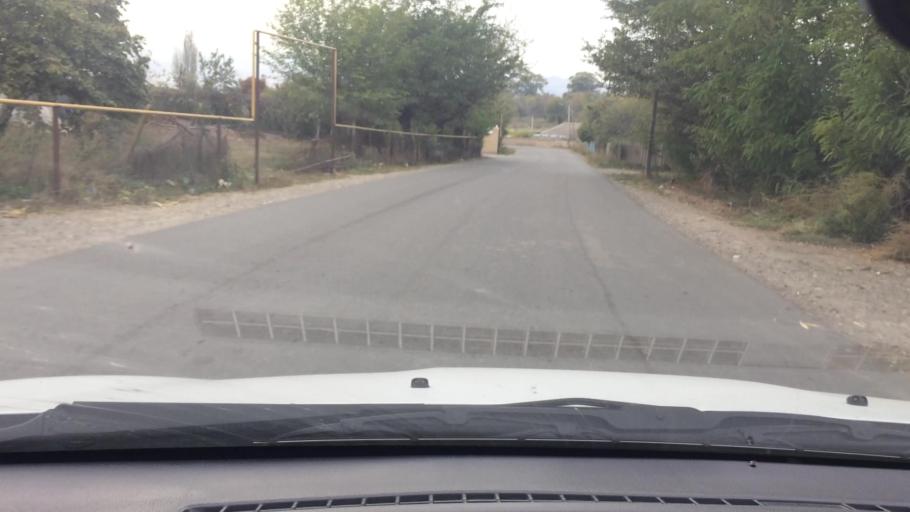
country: AM
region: Tavush
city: Bagratashen
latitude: 41.3406
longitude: 44.8914
